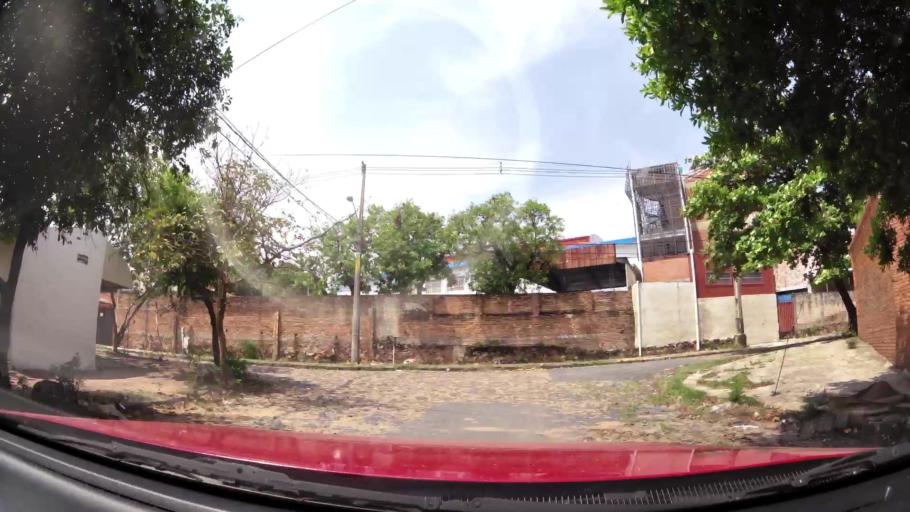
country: PY
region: Asuncion
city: Asuncion
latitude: -25.2755
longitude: -57.6003
